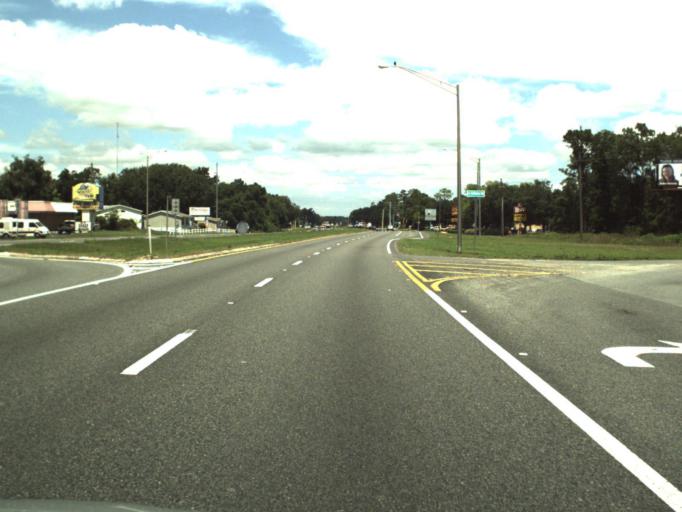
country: US
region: Florida
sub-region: Marion County
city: Ocala
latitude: 29.2180
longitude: -82.1458
